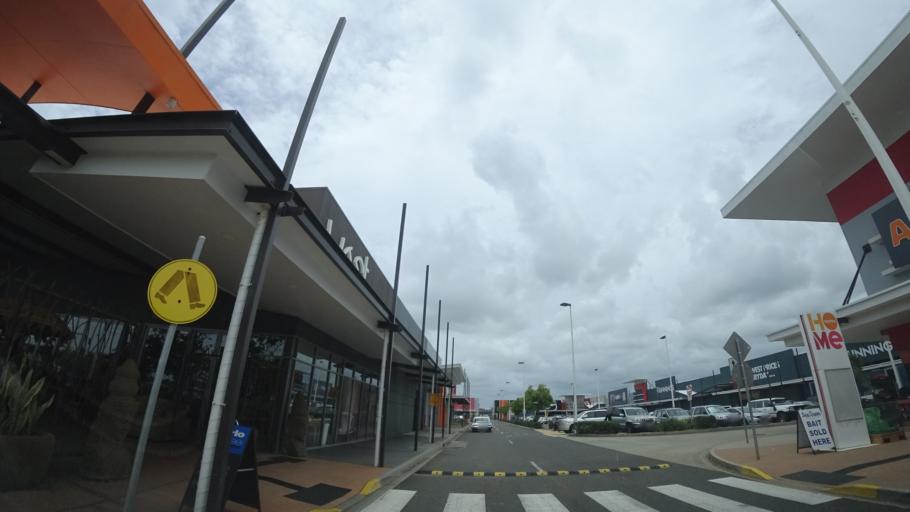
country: AU
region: Queensland
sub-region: Sunshine Coast
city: Dicky Beach
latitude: -26.7363
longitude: 153.1196
